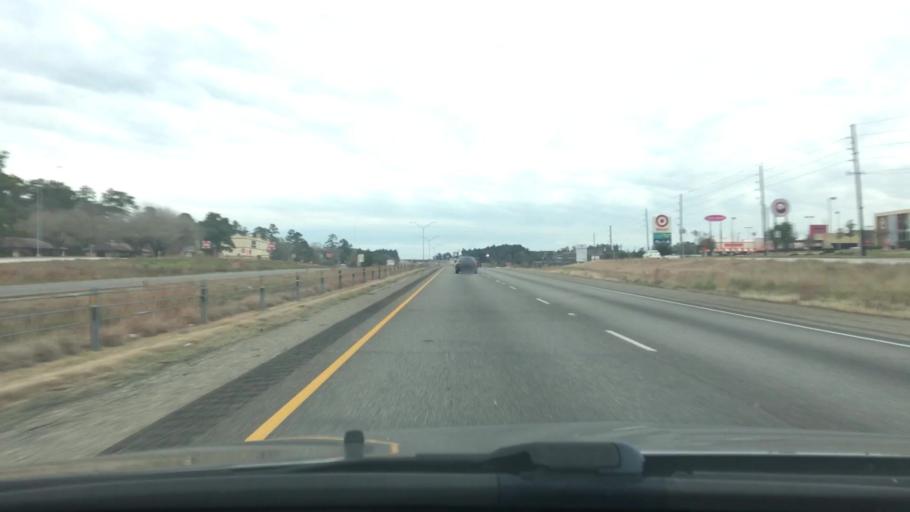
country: US
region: Texas
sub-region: Walker County
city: Huntsville
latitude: 30.7102
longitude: -95.5645
